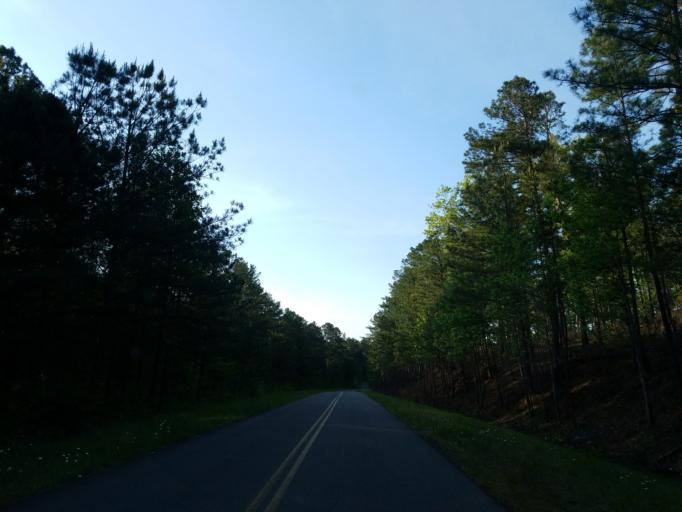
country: US
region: Georgia
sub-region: Gordon County
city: Calhoun
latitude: 34.6092
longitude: -85.0810
